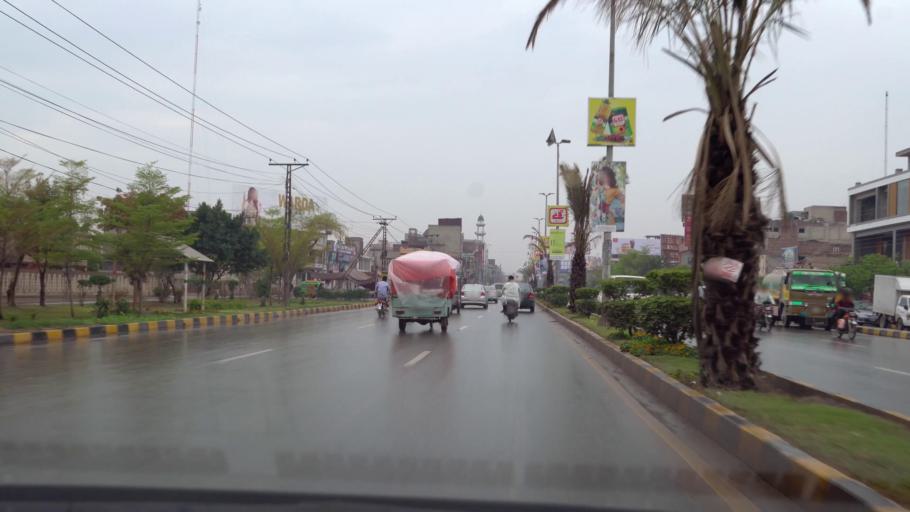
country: PK
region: Punjab
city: Faisalabad
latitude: 31.4041
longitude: 73.1033
